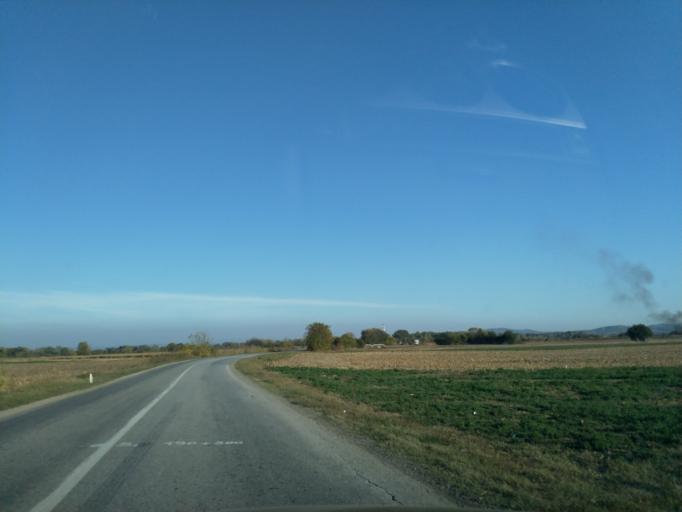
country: RS
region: Central Serbia
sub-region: Pomoravski Okrug
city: Svilajnac
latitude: 44.2375
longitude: 21.1336
